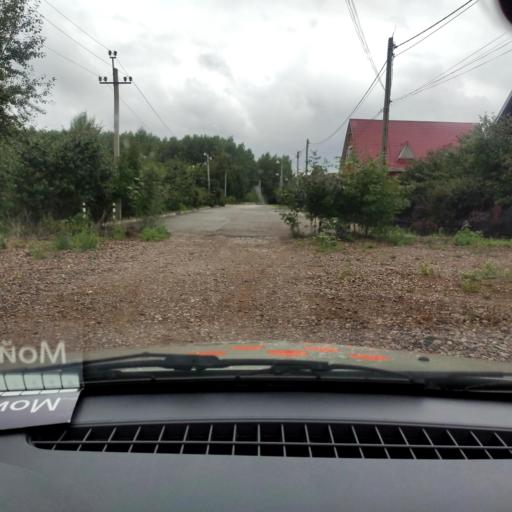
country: RU
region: Bashkortostan
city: Ufa
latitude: 54.7681
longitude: 55.9438
